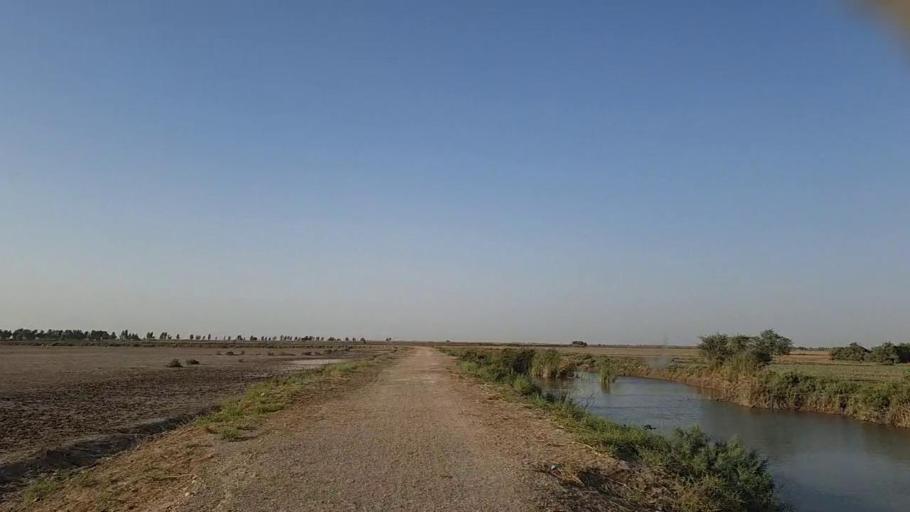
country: PK
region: Sindh
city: Jati
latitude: 24.4196
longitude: 68.2949
